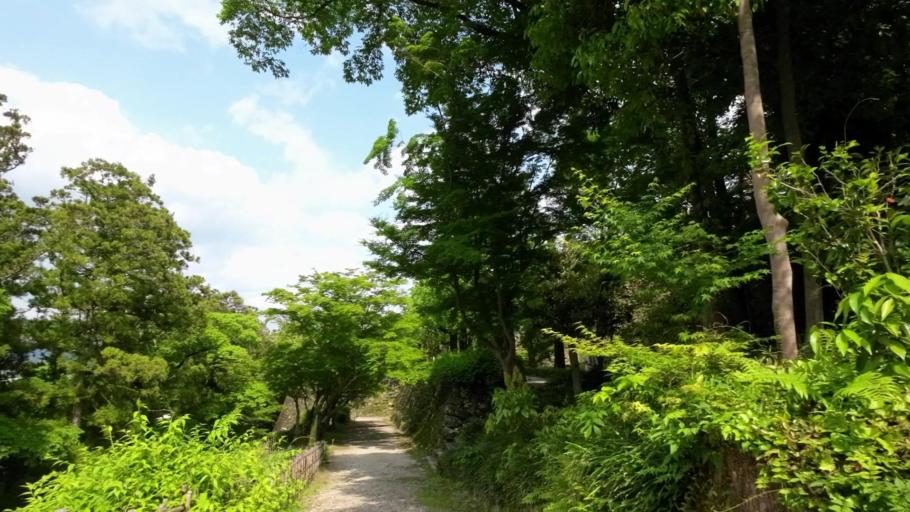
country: JP
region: Kochi
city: Kochi-shi
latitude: 33.5618
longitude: 133.5305
